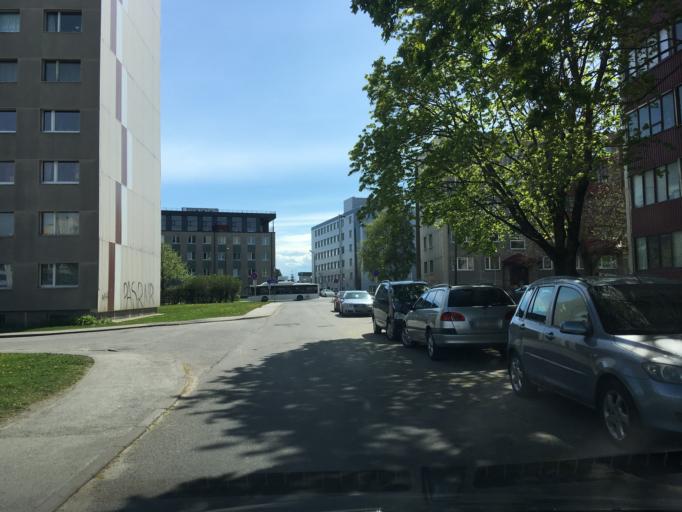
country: EE
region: Harju
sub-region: Tallinna linn
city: Kose
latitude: 59.4338
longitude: 24.8244
